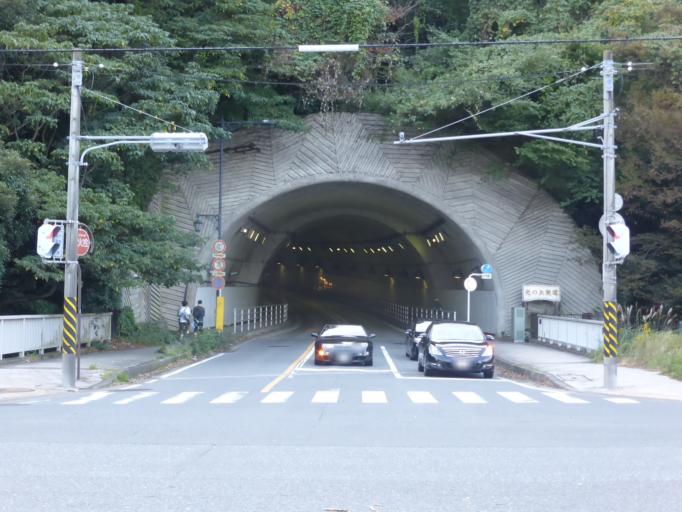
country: JP
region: Kanagawa
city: Yokosuka
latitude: 35.2228
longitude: 139.6842
